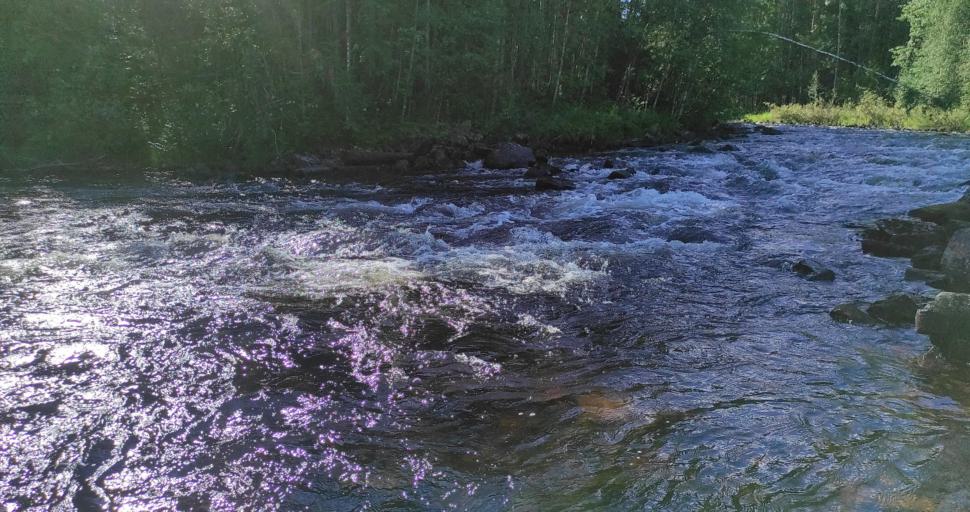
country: RU
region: Murmansk
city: Zelenoborskiy
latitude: 66.5721
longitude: 32.0672
